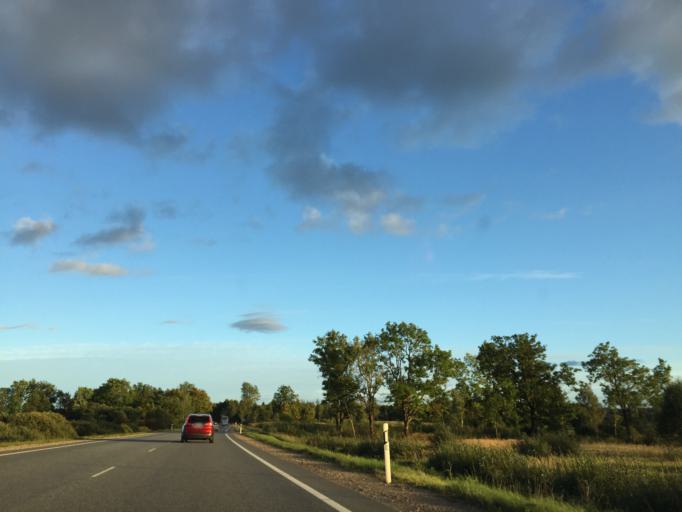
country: LV
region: Broceni
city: Broceni
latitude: 56.6731
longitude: 22.5863
